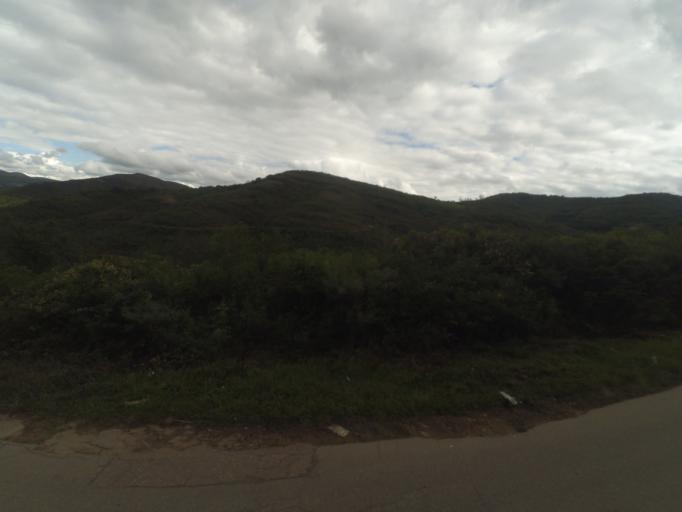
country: BO
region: Santa Cruz
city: Samaipata
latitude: -18.1736
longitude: -63.8477
